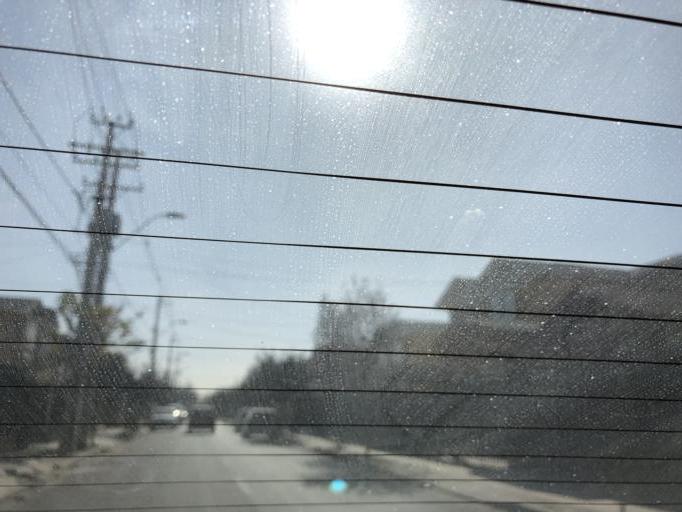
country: CL
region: Santiago Metropolitan
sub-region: Provincia de Cordillera
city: Puente Alto
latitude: -33.6022
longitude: -70.5823
